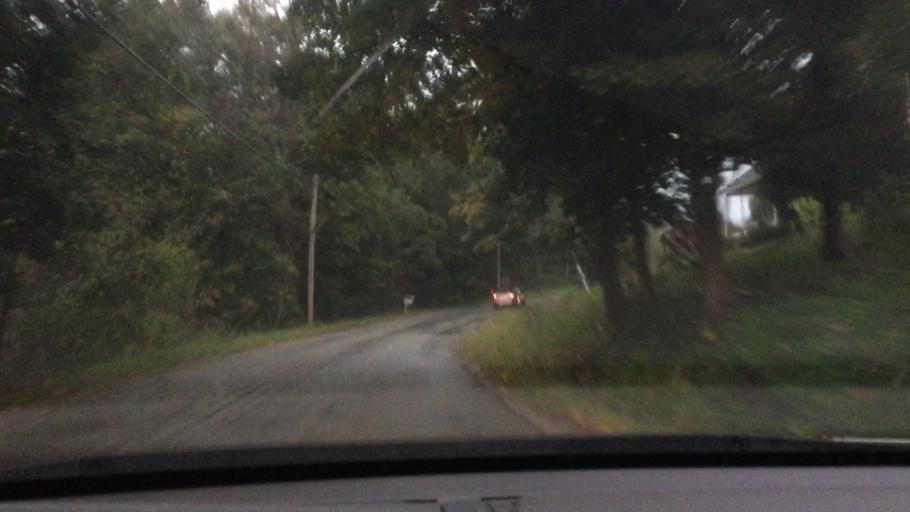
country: US
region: Pennsylvania
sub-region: Washington County
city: Bentleyville
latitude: 40.1284
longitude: -79.9882
